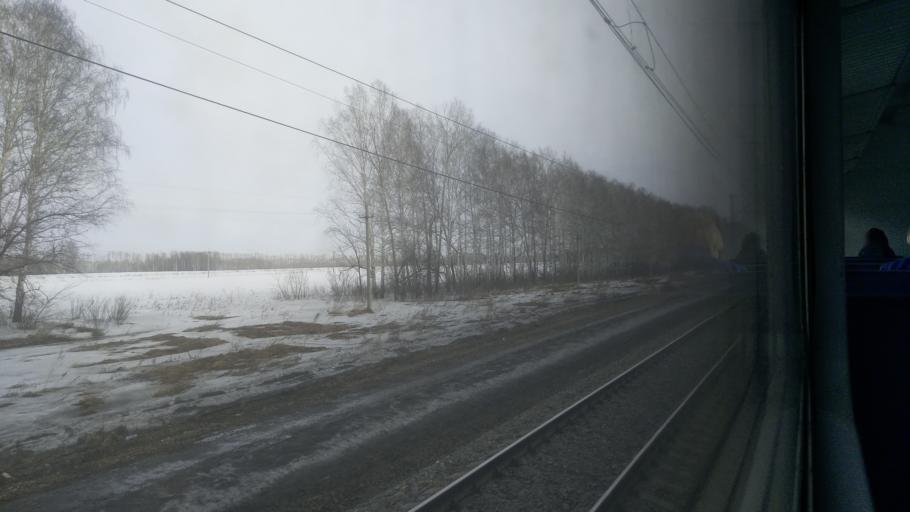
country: RU
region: Novosibirsk
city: Bolotnoye
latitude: 55.7001
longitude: 84.5679
